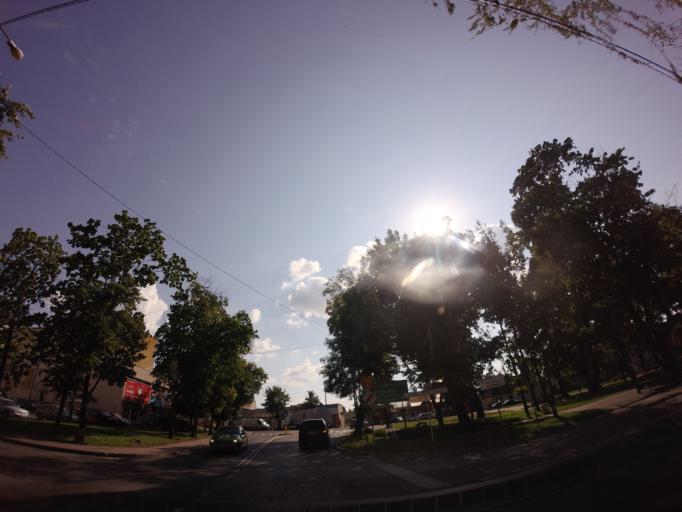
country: PL
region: Masovian Voivodeship
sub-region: Powiat sokolowski
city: Sokolow Podlaski
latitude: 52.4074
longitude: 22.2540
